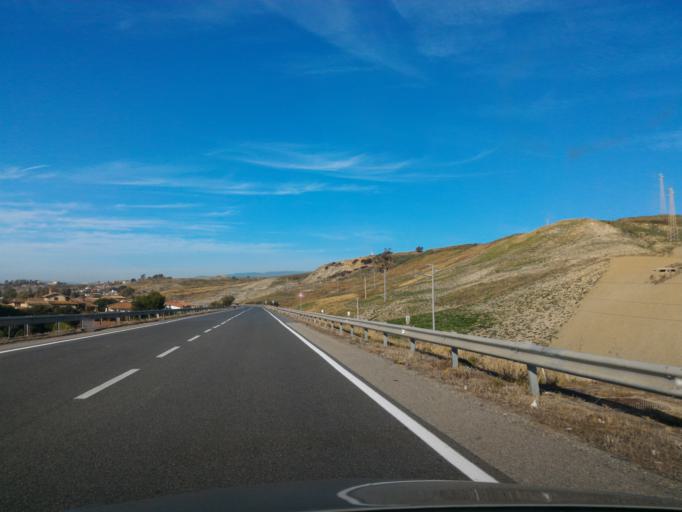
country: IT
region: Calabria
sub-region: Provincia di Crotone
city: Le Castella
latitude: 38.9397
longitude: 16.9857
